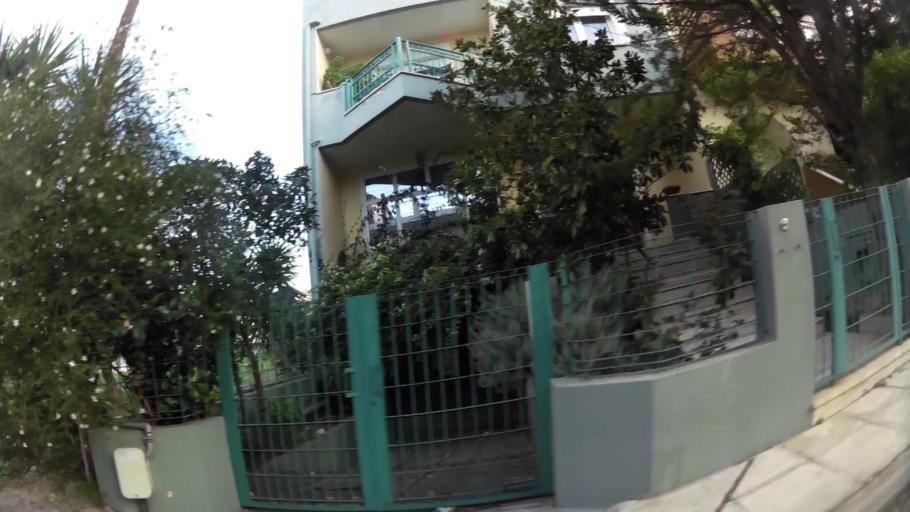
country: GR
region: Attica
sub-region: Nomarchia Athinas
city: Vrilissia
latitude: 38.0412
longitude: 23.8211
